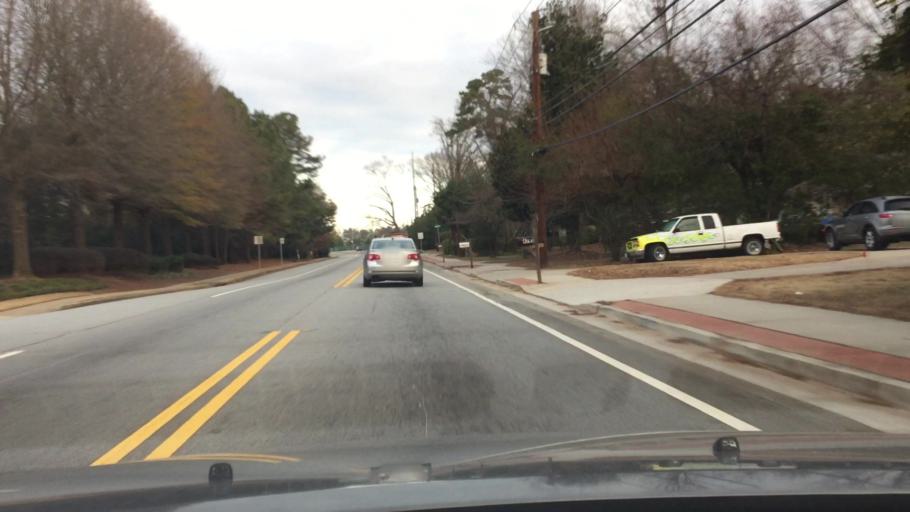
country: US
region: Georgia
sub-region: DeKalb County
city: Doraville
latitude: 33.9346
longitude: -84.2664
